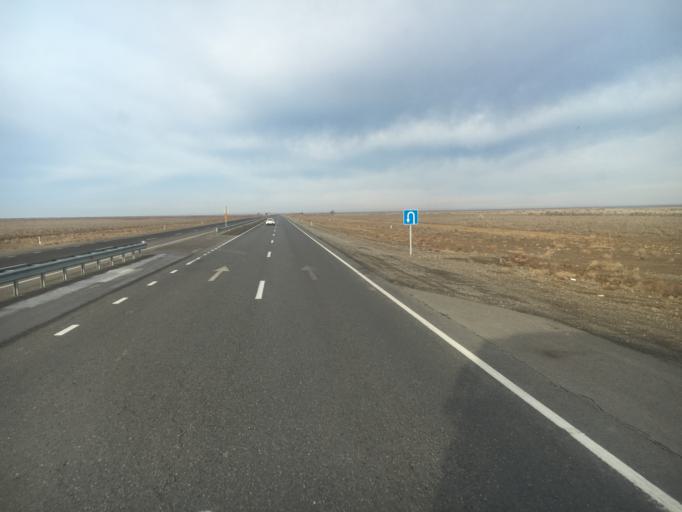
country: KZ
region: Ongtustik Qazaqstan
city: Turkestan
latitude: 43.5180
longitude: 67.8094
